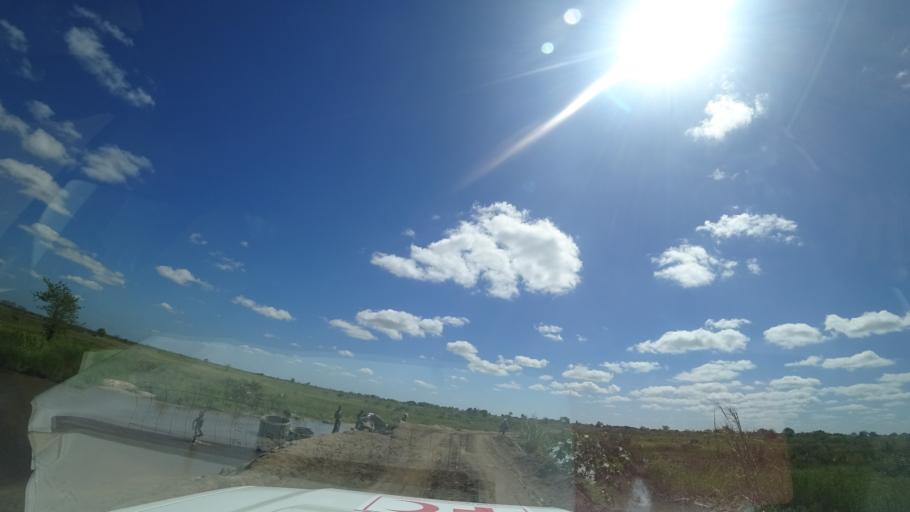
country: MZ
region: Sofala
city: Dondo
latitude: -19.4683
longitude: 34.5981
